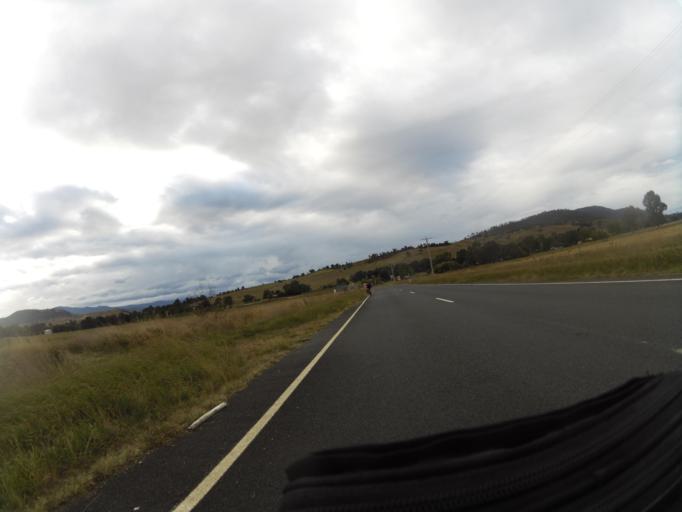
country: AU
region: New South Wales
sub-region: Snowy River
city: Jindabyne
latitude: -36.1220
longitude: 147.9836
